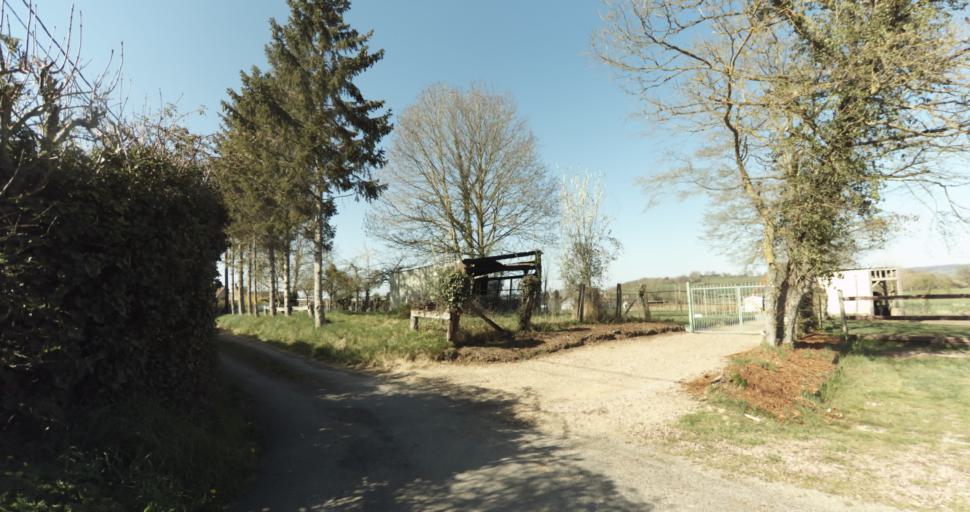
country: FR
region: Lower Normandy
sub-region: Departement du Calvados
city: Saint-Pierre-sur-Dives
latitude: 48.9431
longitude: -0.0038
